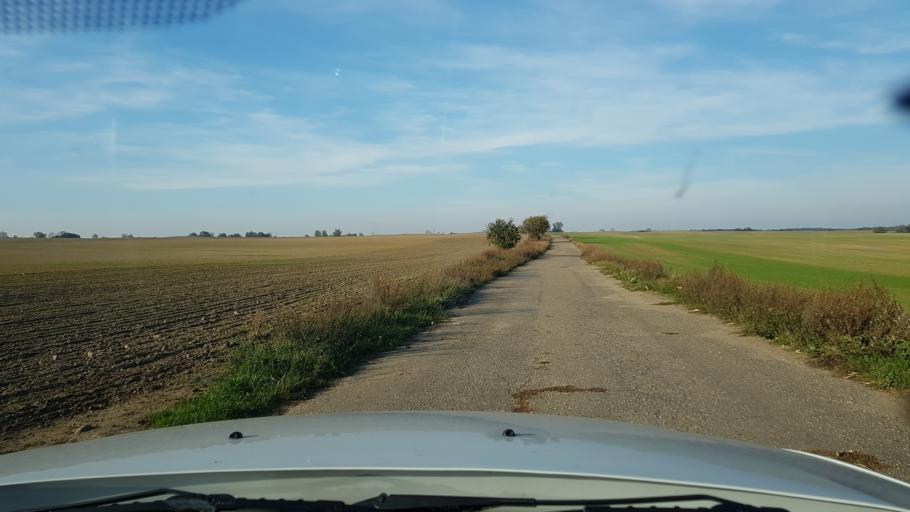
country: PL
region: West Pomeranian Voivodeship
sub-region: Powiat gryfinski
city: Moryn
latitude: 52.8774
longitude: 14.3118
